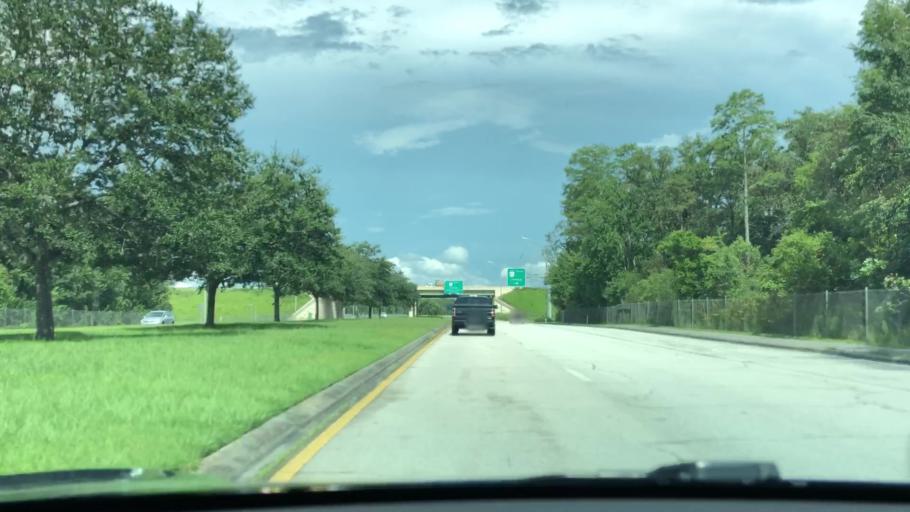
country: US
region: Florida
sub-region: Orange County
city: Azalea Park
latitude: 28.4778
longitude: -81.2420
